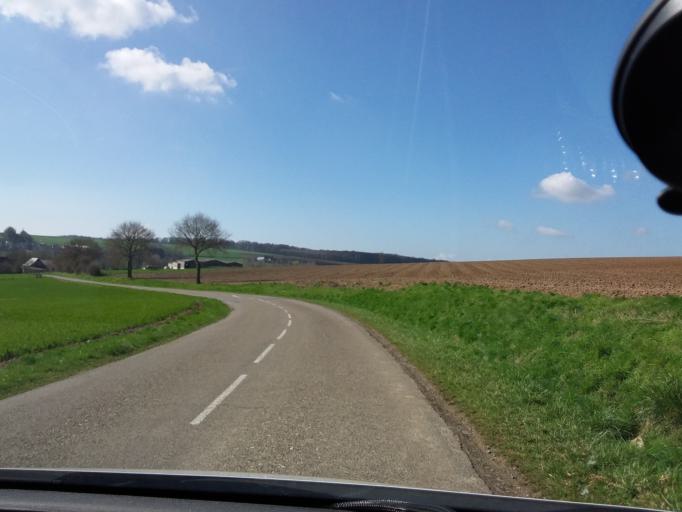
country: FR
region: Picardie
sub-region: Departement de l'Aisne
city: Montcornet
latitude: 49.7886
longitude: 4.0064
